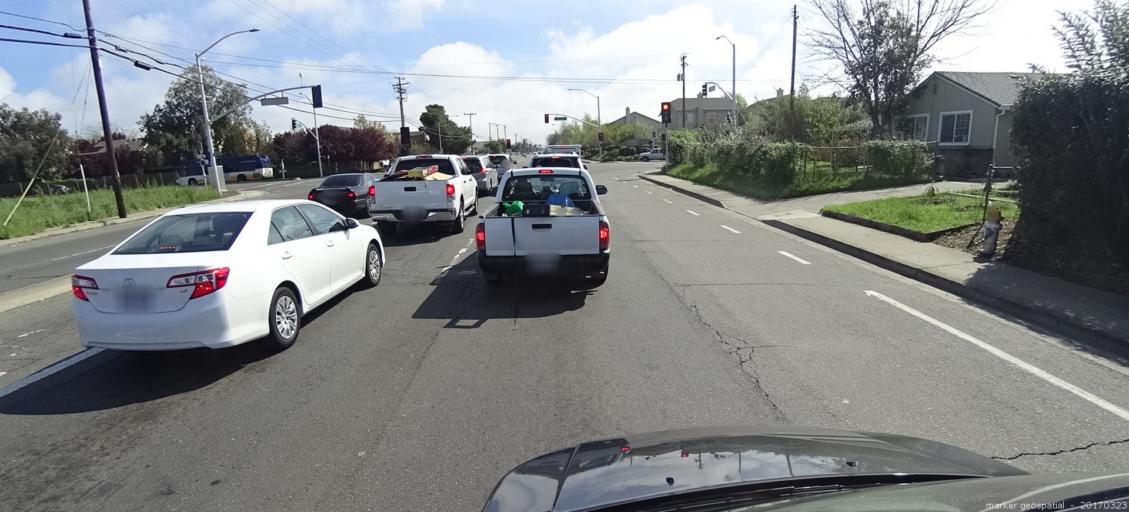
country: US
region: California
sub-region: Sacramento County
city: Florin
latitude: 38.5105
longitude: -121.4281
